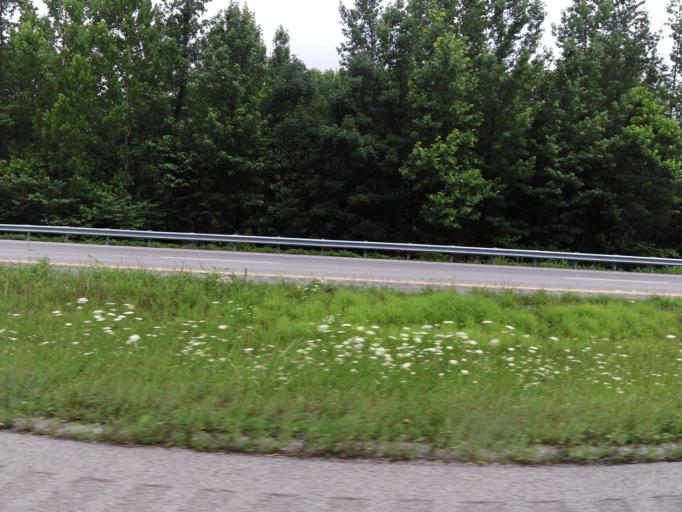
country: US
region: Kentucky
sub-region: Muhlenberg County
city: Central City
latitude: 37.3202
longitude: -87.0134
